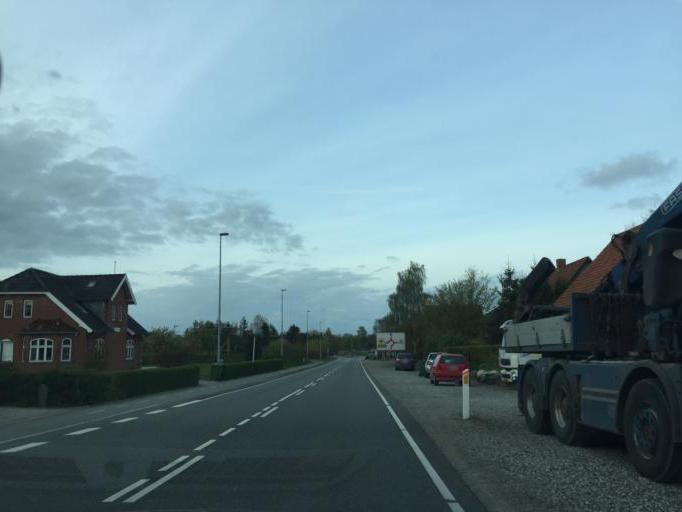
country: DK
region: South Denmark
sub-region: Faaborg-Midtfyn Kommune
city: Ringe
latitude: 55.1799
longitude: 10.5274
